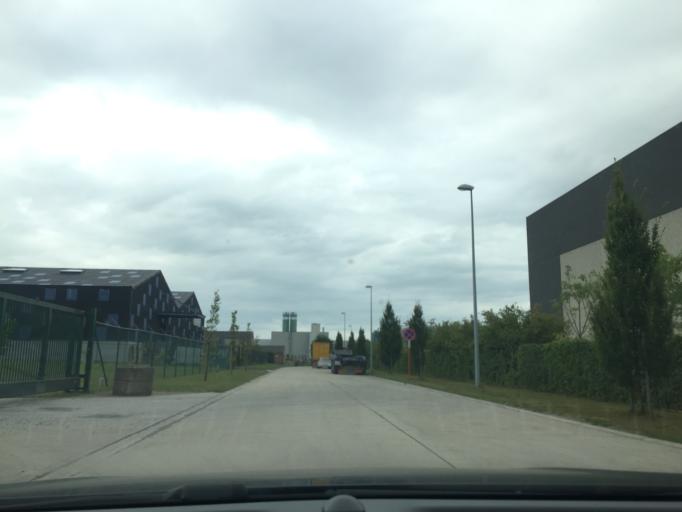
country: BE
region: Flanders
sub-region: Provincie West-Vlaanderen
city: Roeselare
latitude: 50.9364
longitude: 3.1605
